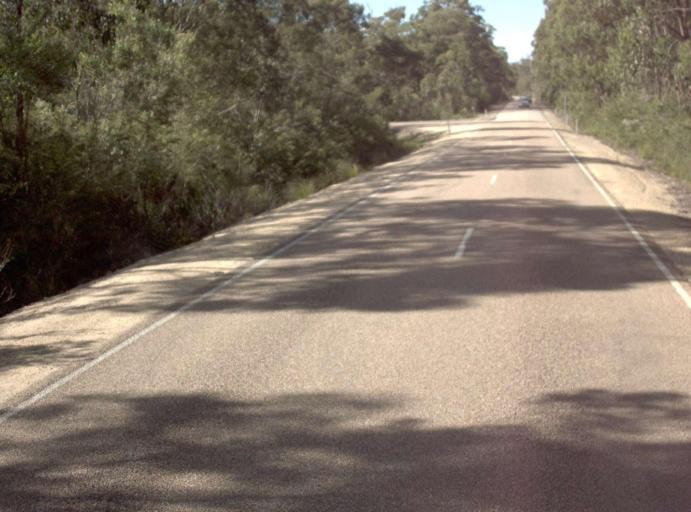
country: AU
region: Victoria
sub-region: East Gippsland
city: Lakes Entrance
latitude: -37.6249
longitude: 148.1113
